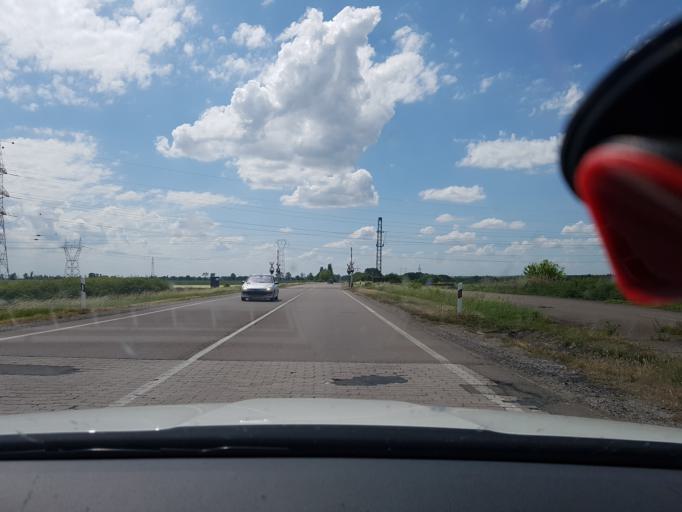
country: HU
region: Heves
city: Domoszlo
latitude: 47.7415
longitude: 20.1336
